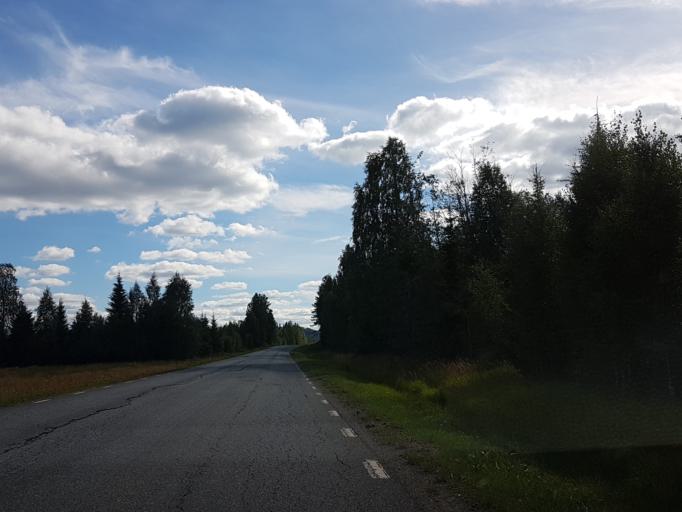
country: SE
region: Vaesterbotten
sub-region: Skelleftea Kommun
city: Burtraesk
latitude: 64.3102
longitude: 20.5318
